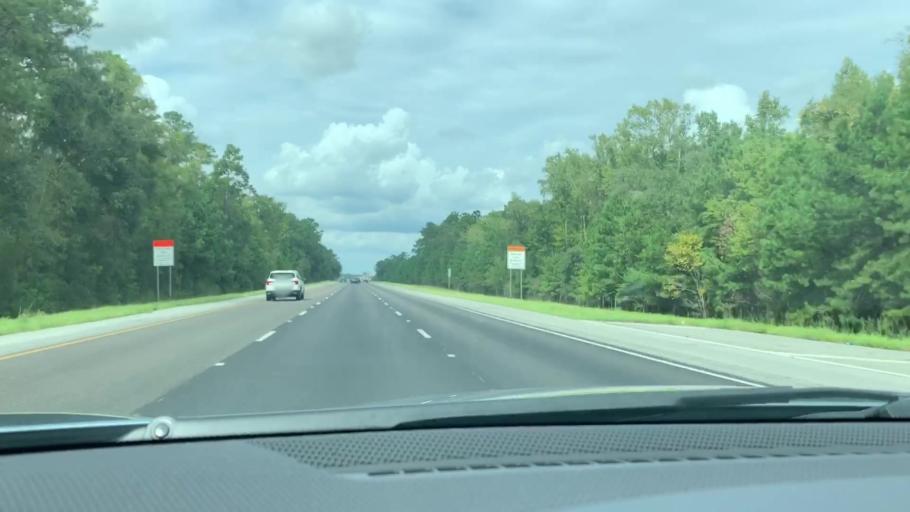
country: US
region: Georgia
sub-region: Liberty County
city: Midway
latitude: 31.7202
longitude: -81.3890
